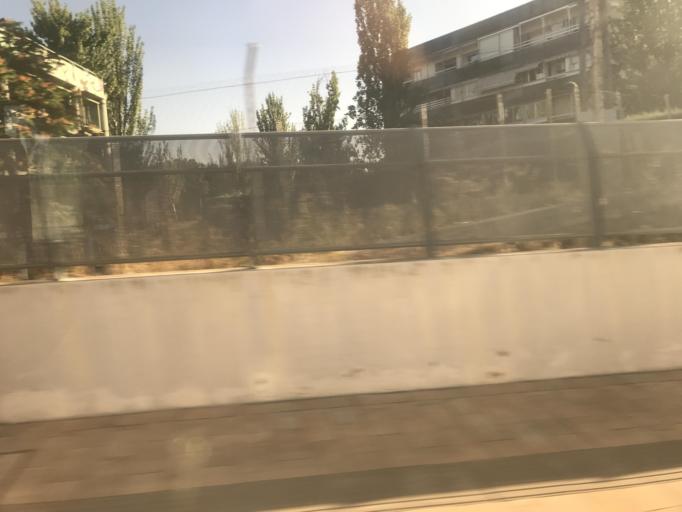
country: ES
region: Madrid
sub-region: Provincia de Madrid
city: Majadahonda
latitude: 40.4738
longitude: -3.8443
